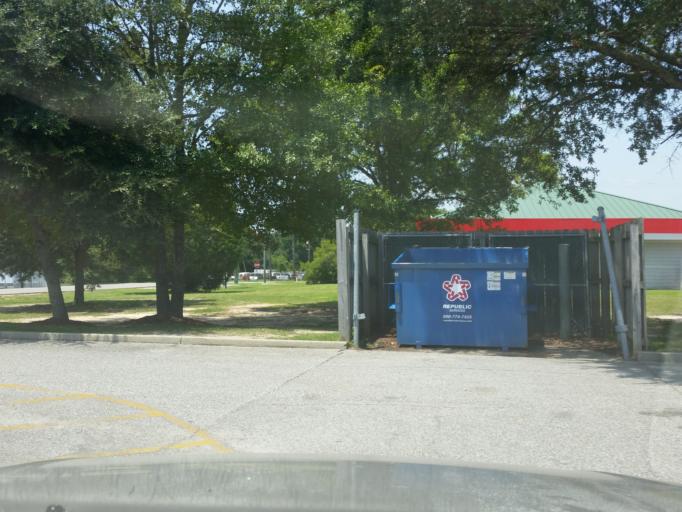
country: US
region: Florida
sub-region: Escambia County
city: Brent
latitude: 30.4803
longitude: -87.2588
